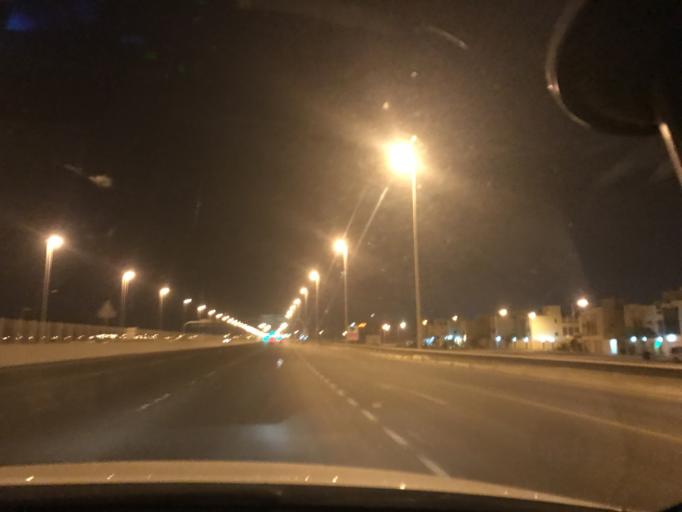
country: BH
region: Muharraq
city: Al Muharraq
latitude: 26.2869
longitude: 50.6388
